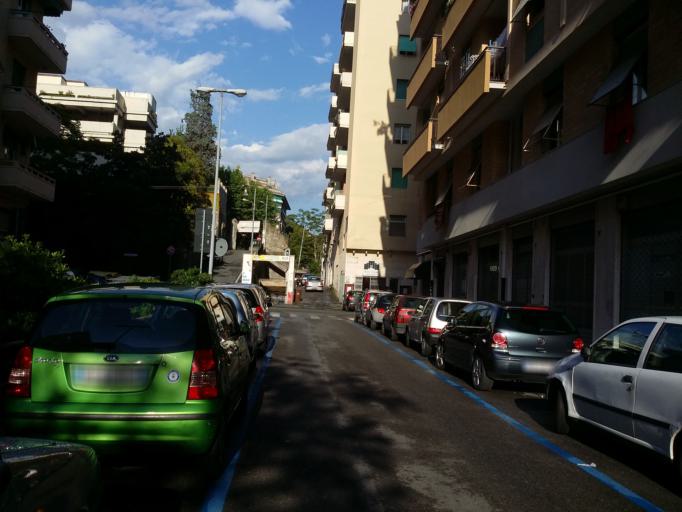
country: IT
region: Liguria
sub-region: Provincia di Genova
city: Genoa
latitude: 44.4081
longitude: 8.9583
